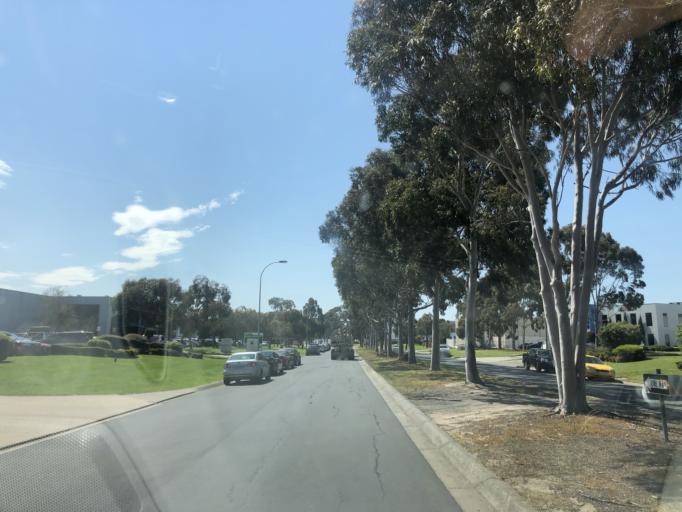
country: AU
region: Victoria
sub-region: Casey
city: Hampton Park
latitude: -38.0316
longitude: 145.2288
